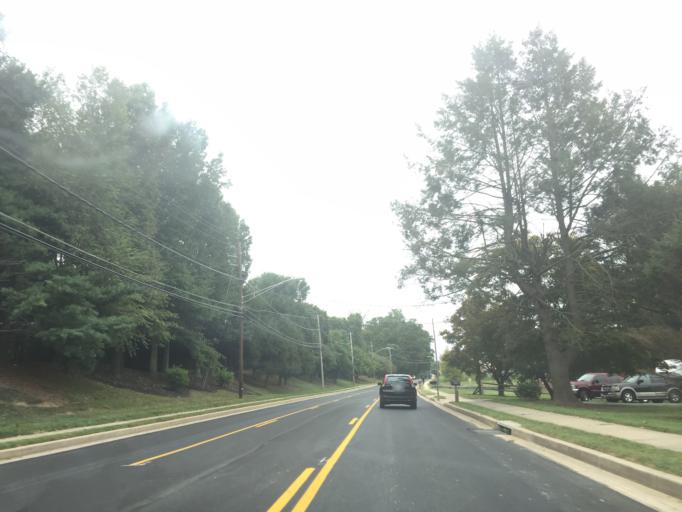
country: US
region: Maryland
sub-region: Harford County
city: South Bel Air
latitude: 39.5126
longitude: -76.3478
